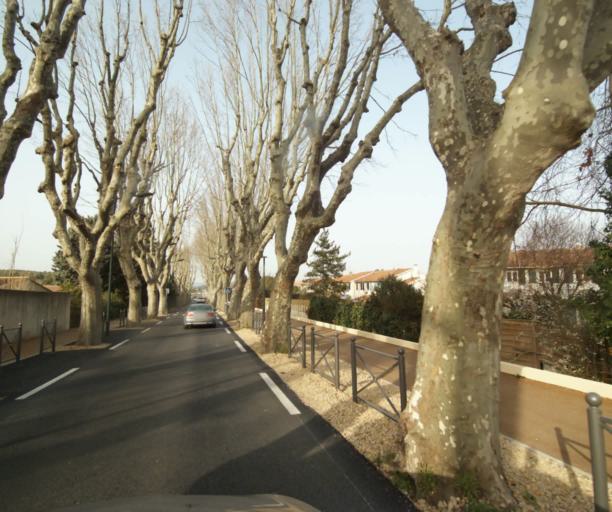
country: FR
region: Provence-Alpes-Cote d'Azur
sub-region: Departement des Bouches-du-Rhone
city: Cabries
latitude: 43.4620
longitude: 5.3532
